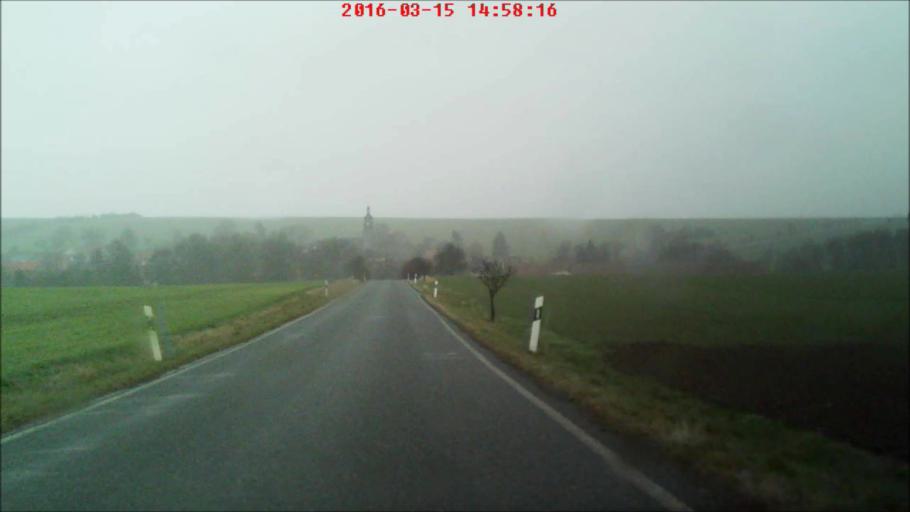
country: DE
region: Thuringia
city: Rockhausen
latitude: 50.9076
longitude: 11.0366
